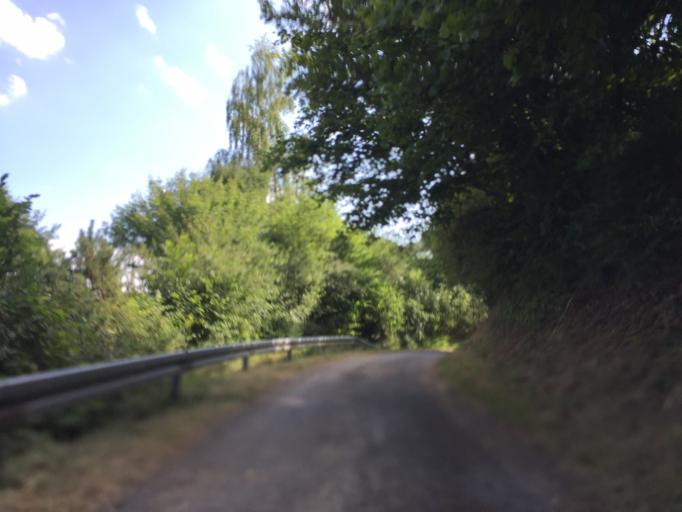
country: DE
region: Hesse
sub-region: Regierungsbezirk Giessen
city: Heuchelheim
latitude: 50.6128
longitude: 8.6259
